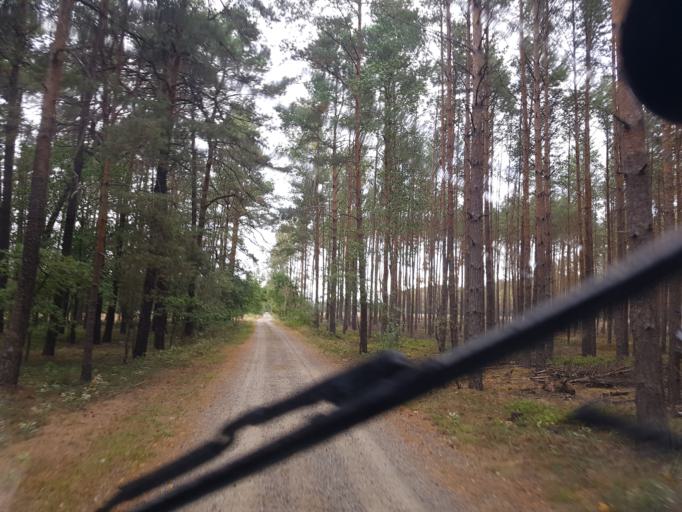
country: DE
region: Brandenburg
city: Finsterwalde
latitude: 51.6164
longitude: 13.7762
